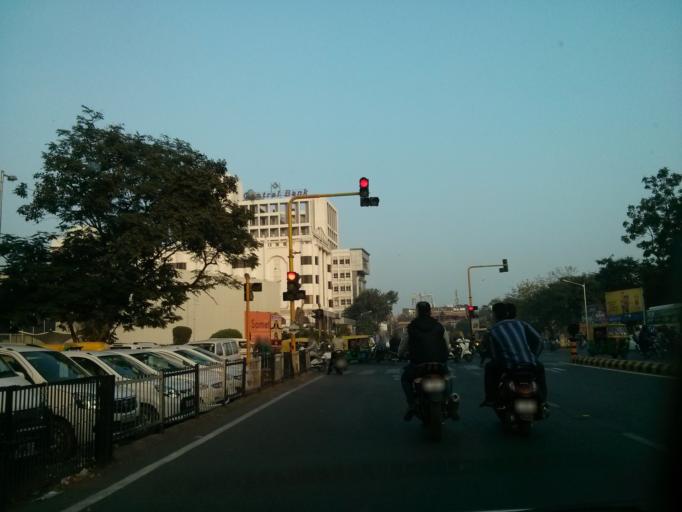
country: IN
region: Gujarat
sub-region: Ahmadabad
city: Ahmedabad
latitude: 23.0273
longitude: 72.5791
